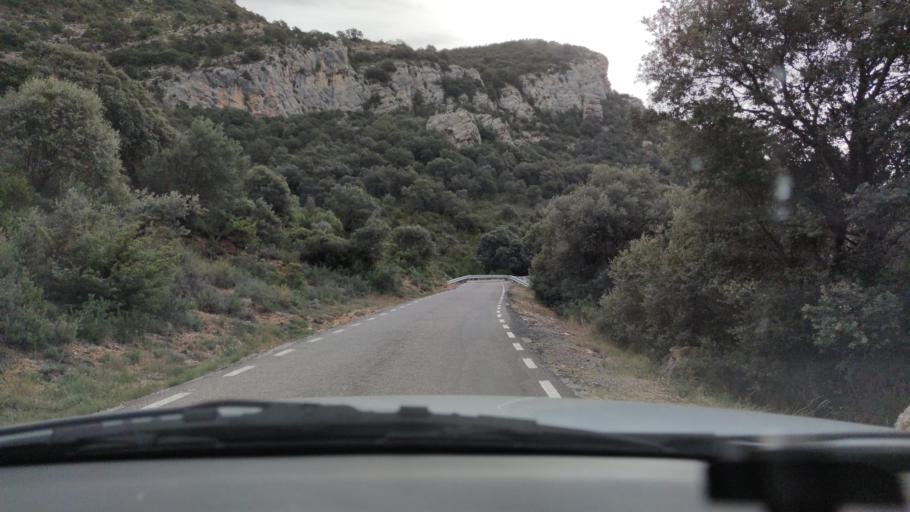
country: ES
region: Catalonia
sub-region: Provincia de Lleida
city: Artesa de Segre
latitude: 42.0192
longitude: 1.0326
